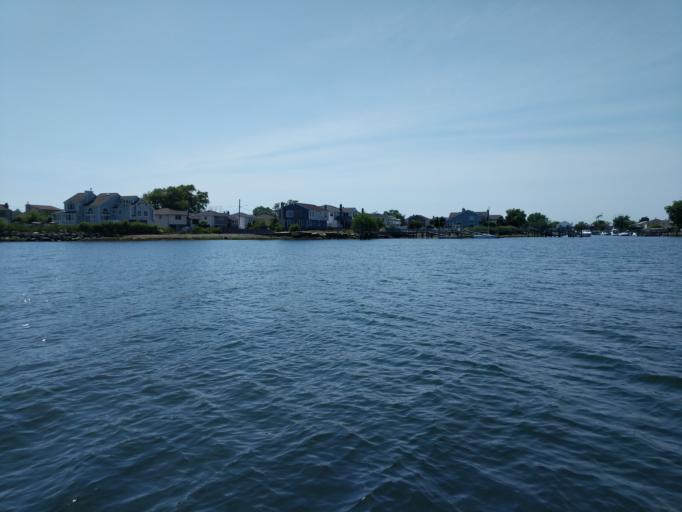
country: US
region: New York
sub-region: Nassau County
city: Barnum Island
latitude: 40.6027
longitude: -73.6440
